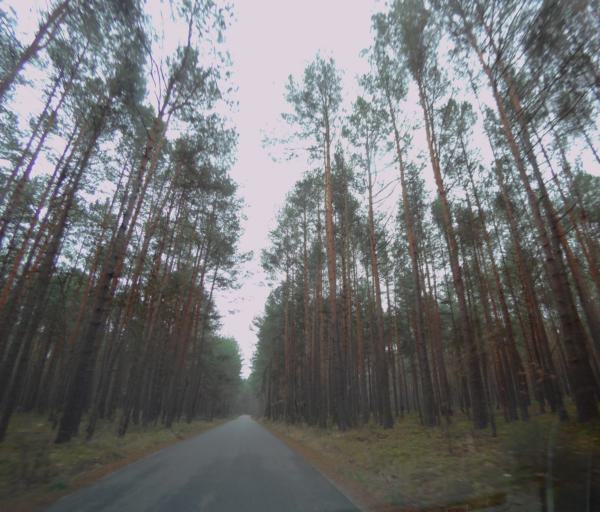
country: PL
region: Subcarpathian Voivodeship
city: Nowa Sarzyna
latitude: 50.3065
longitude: 22.3457
